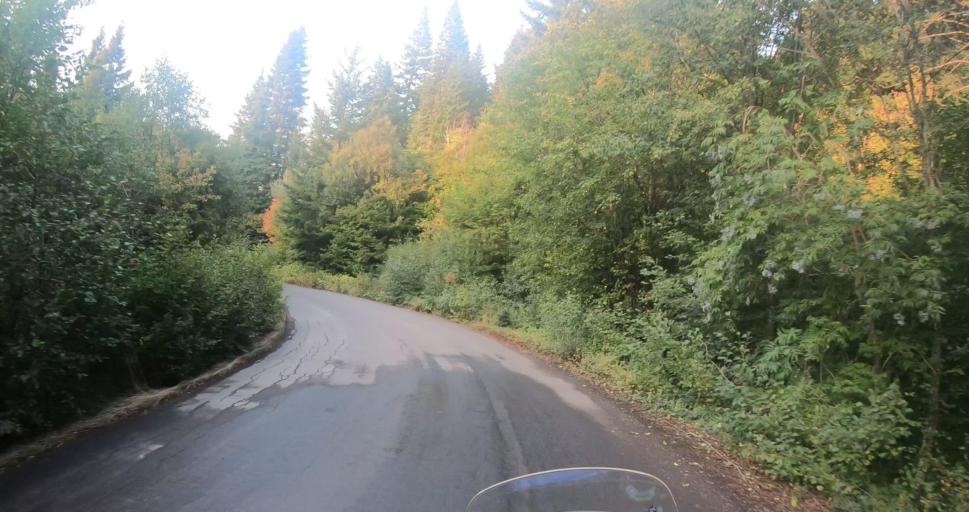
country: US
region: Oregon
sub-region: Hood River County
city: Odell
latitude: 45.4598
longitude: -121.6290
